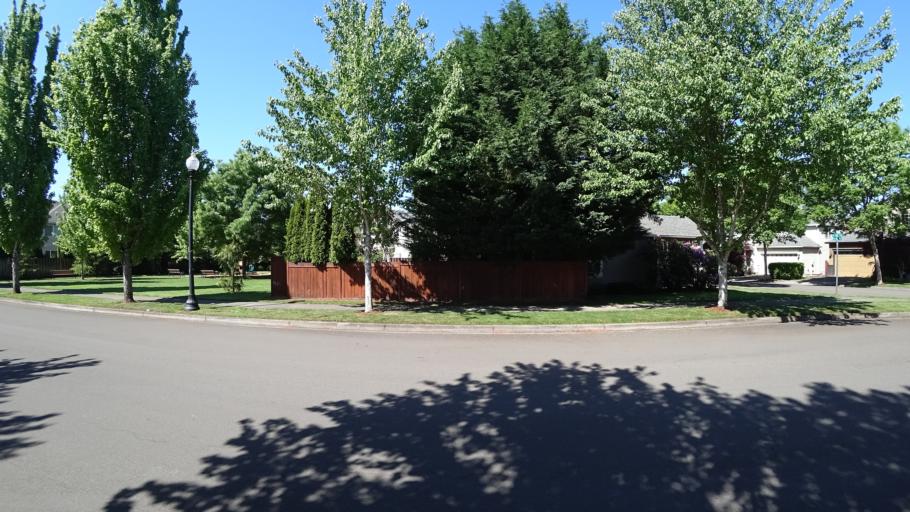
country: US
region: Oregon
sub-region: Washington County
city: Rockcreek
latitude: 45.5271
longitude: -122.9199
